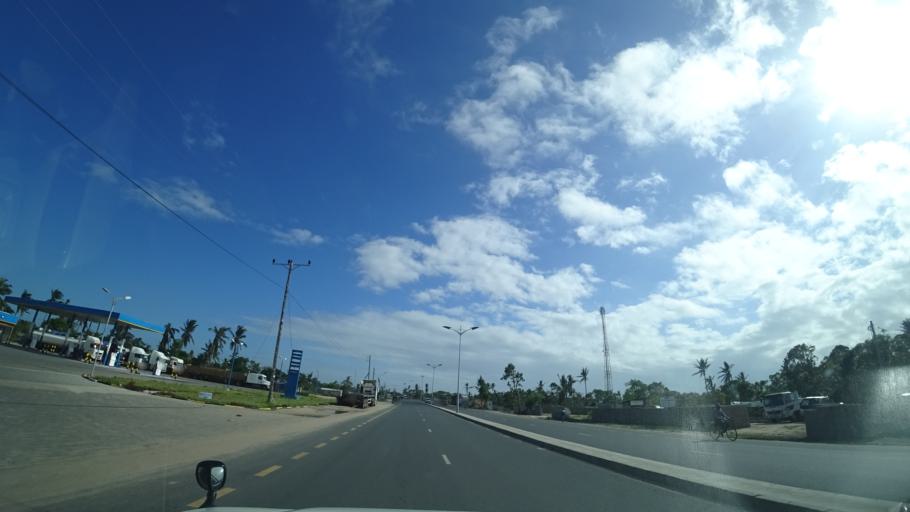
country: MZ
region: Sofala
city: Beira
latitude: -19.7539
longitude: 34.8766
